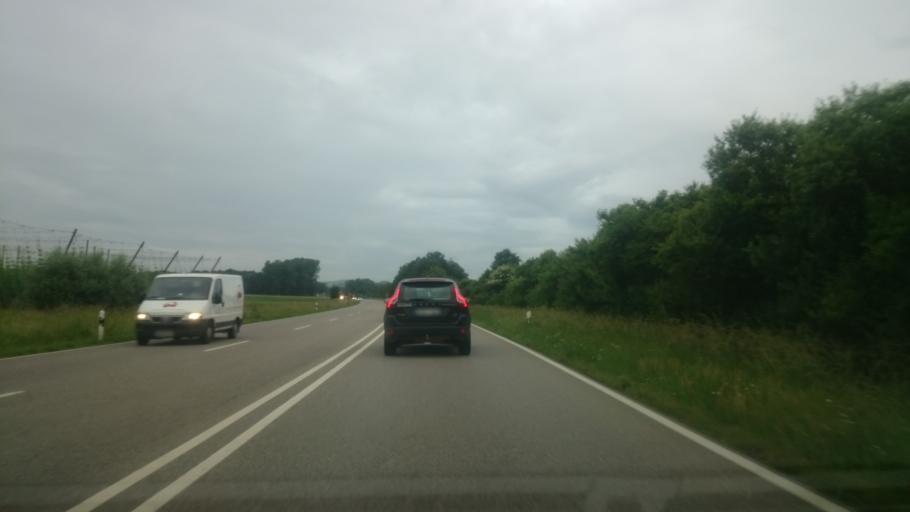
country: DE
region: Bavaria
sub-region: Upper Bavaria
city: Reichertshofen
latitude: 48.6496
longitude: 11.4954
